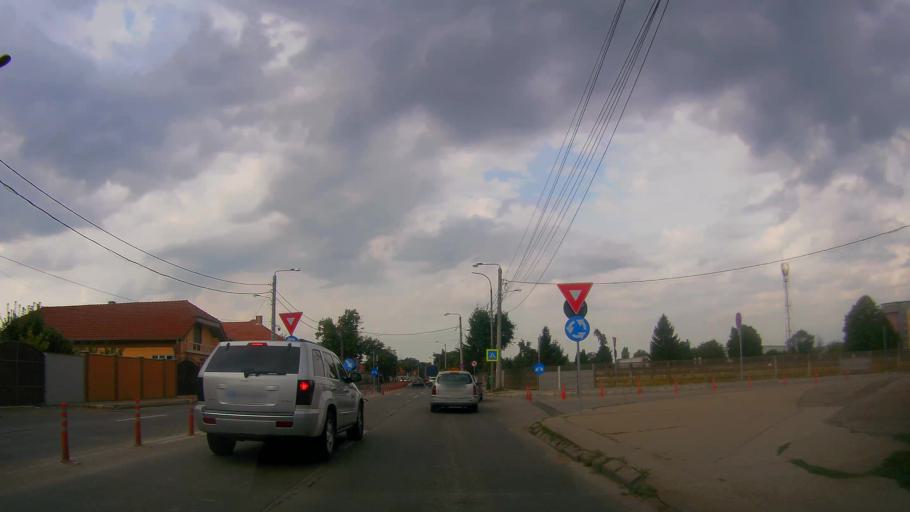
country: RO
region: Satu Mare
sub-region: Municipiul Satu Mare
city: Satu Mare
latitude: 47.7917
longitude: 22.8920
